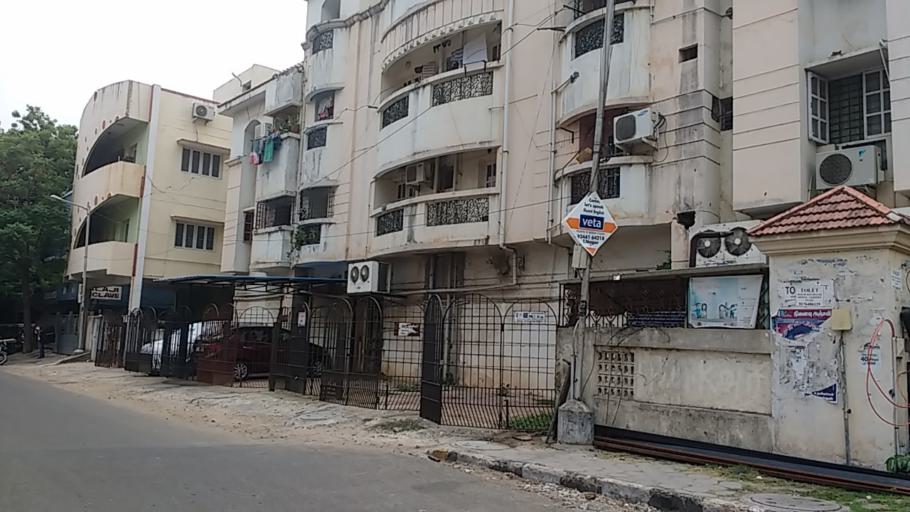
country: IN
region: Tamil Nadu
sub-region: Chennai
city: Chetput
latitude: 13.0516
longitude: 80.2273
